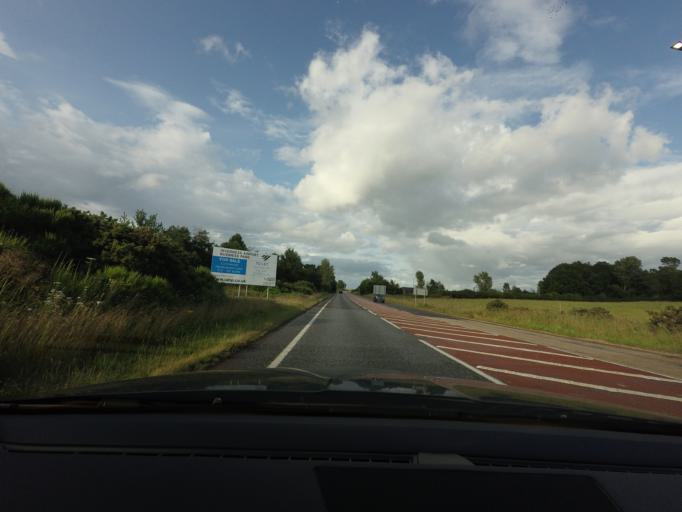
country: GB
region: Scotland
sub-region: Highland
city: Fortrose
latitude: 57.5310
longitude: -4.0472
